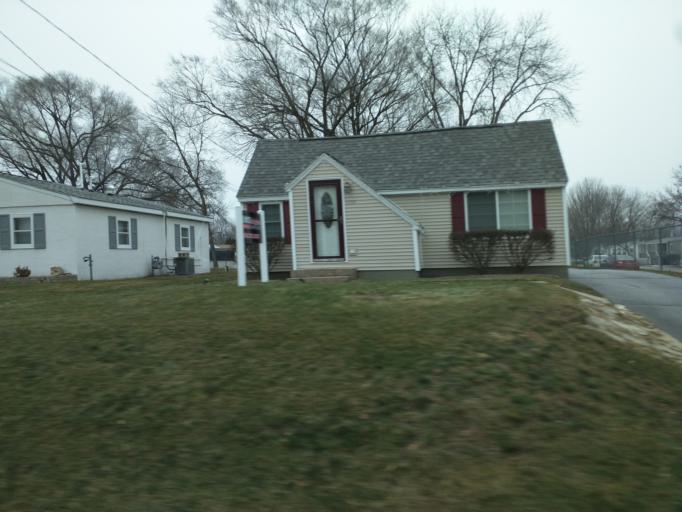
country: US
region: Wisconsin
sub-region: La Crosse County
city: French Island
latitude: 43.8502
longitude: -91.2674
